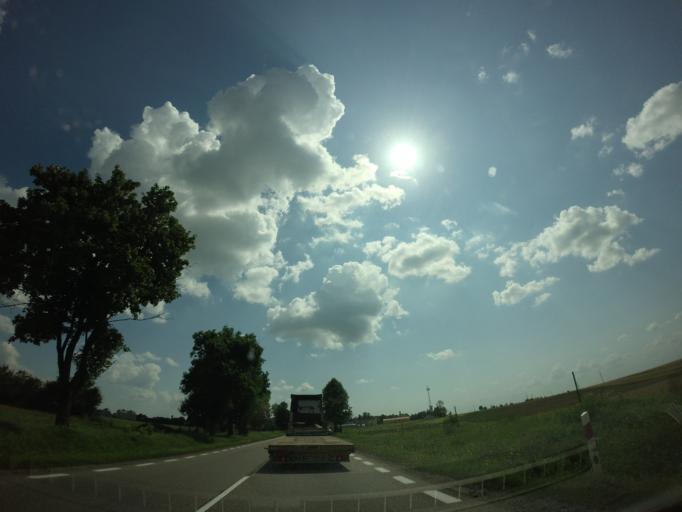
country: PL
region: Podlasie
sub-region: Powiat lomzynski
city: Piatnica
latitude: 53.2154
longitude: 22.1059
